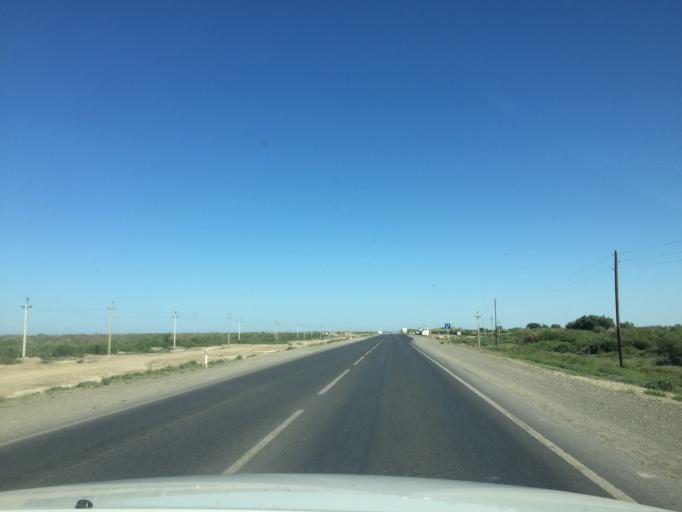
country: KZ
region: Qyzylorda
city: Kyzyl-Orda
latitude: 44.7973
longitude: 65.4518
